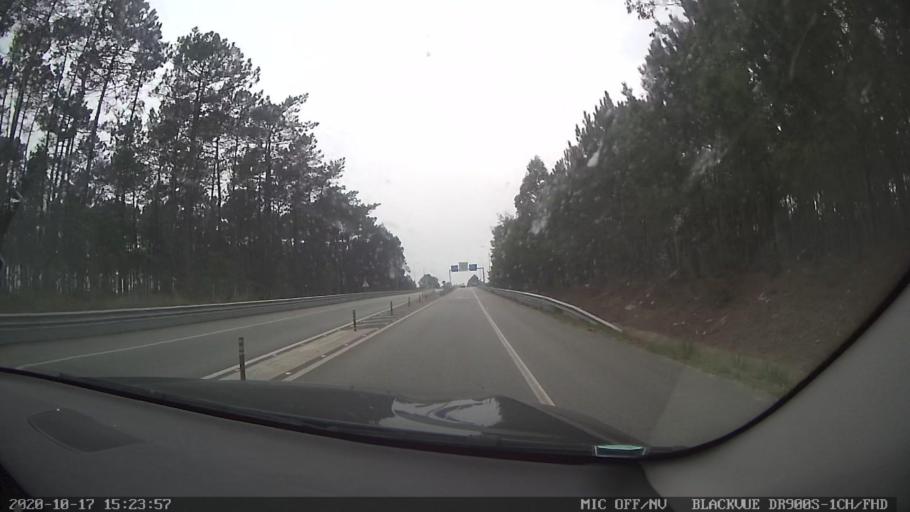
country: PT
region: Braga
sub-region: Esposende
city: Esposende
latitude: 41.5290
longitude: -8.7472
